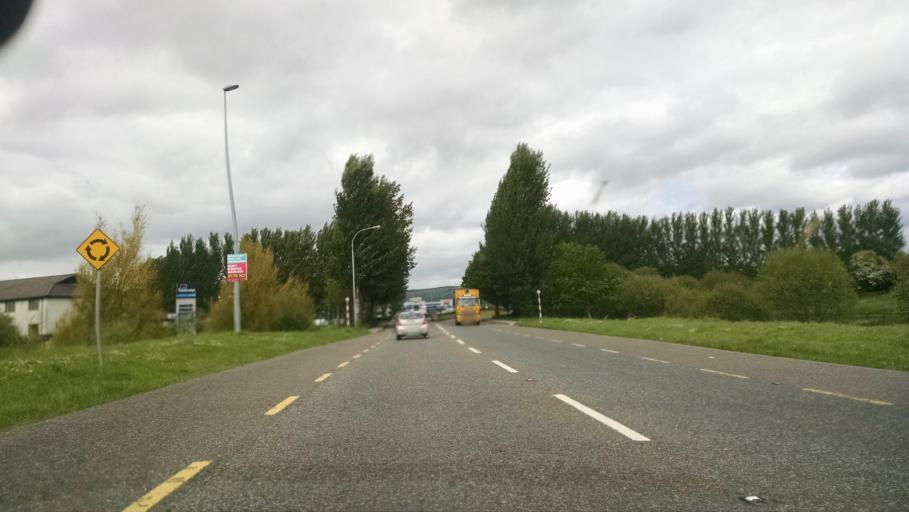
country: IE
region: Munster
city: Moyross
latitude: 52.6723
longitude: -8.6751
